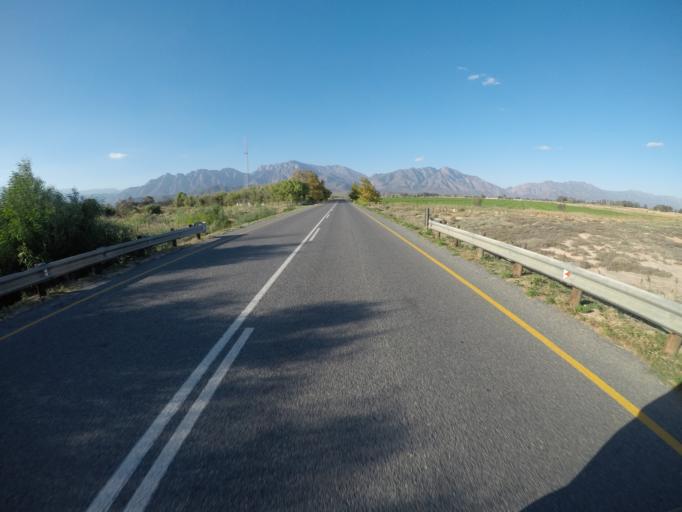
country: ZA
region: Western Cape
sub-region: Cape Winelands District Municipality
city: Worcester
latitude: -33.6771
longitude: 19.5296
